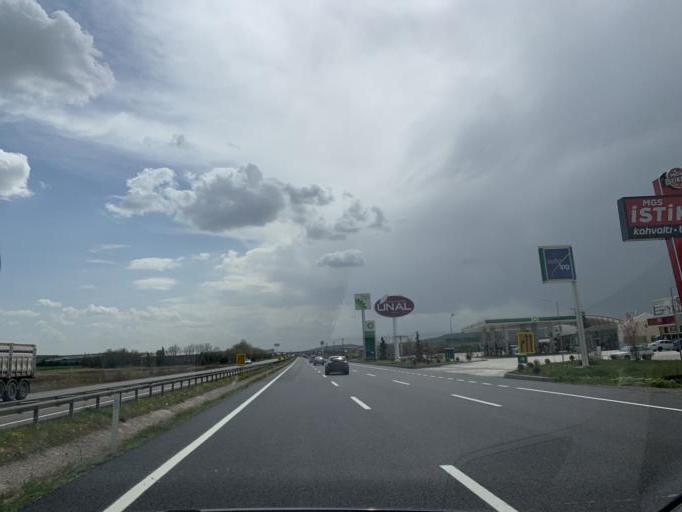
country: TR
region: Ankara
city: Polatli
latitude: 39.6606
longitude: 32.2221
